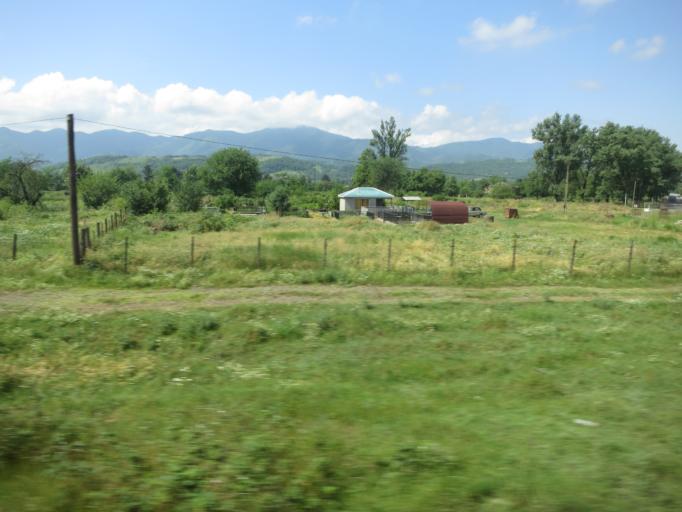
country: GE
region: Imereti
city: Zestap'oni
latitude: 42.1209
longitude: 43.0065
